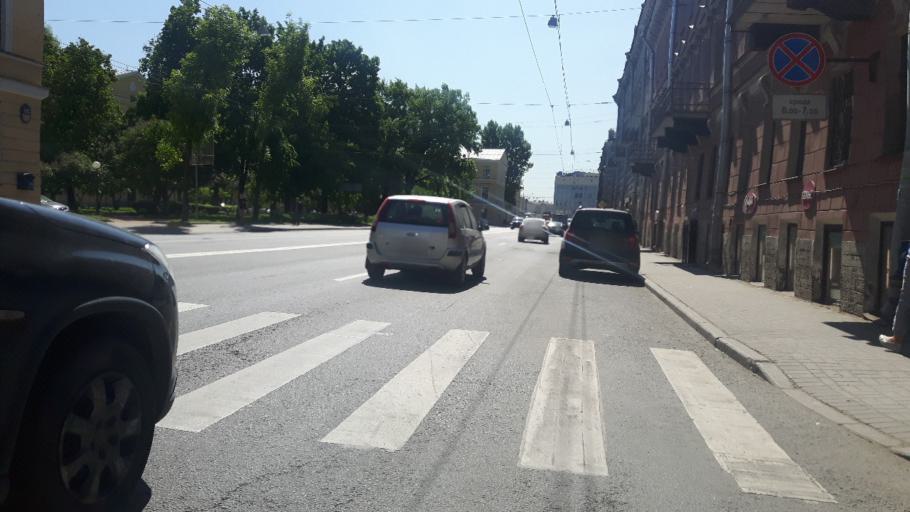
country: RU
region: St.-Petersburg
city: Admiralteisky
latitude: 59.9115
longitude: 30.2975
